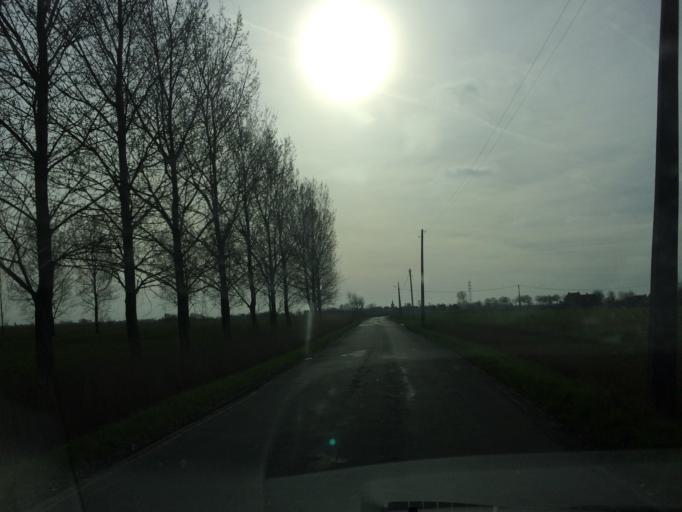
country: BE
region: Flanders
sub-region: Provincie West-Vlaanderen
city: Diksmuide
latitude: 51.0821
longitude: 2.8128
